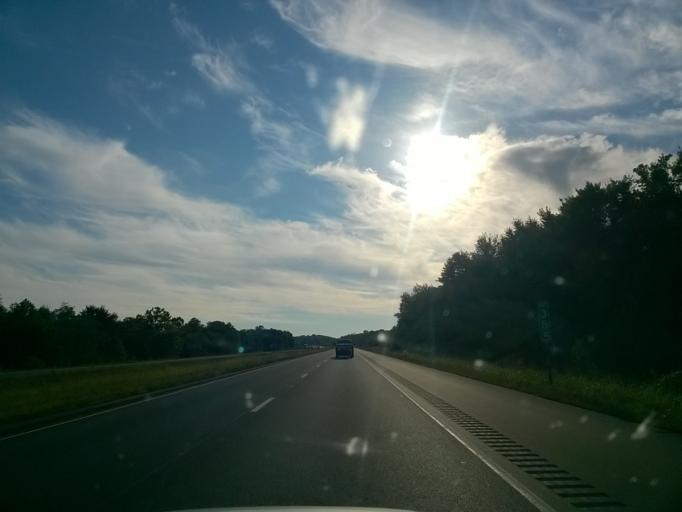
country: US
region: Indiana
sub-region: Warrick County
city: Boonville
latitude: 38.1921
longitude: -87.3068
